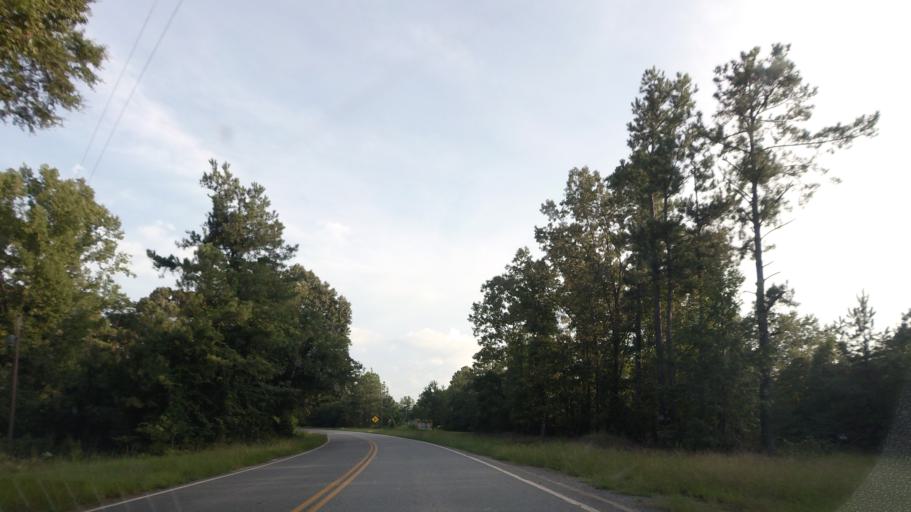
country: US
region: Georgia
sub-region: Wilkinson County
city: Gordon
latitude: 32.8568
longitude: -83.3484
